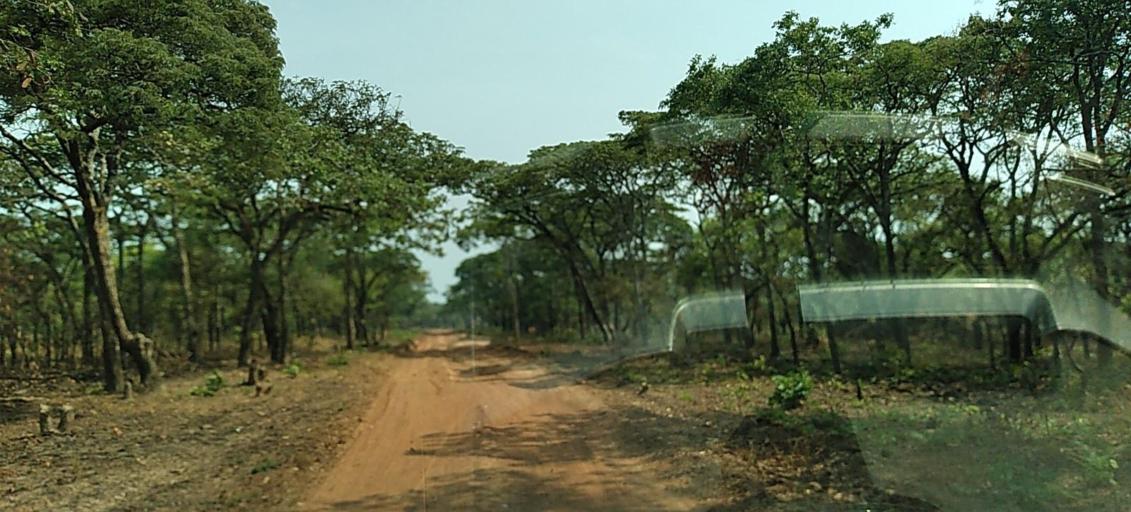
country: ZM
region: North-Western
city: Kansanshi
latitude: -12.0808
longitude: 26.8882
